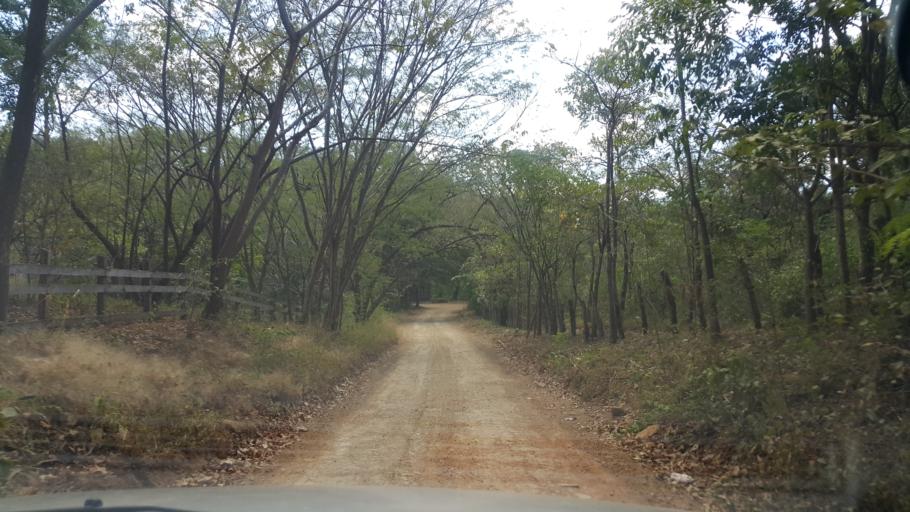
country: NI
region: Rivas
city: San Juan del Sur
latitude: 11.3055
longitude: -85.9101
